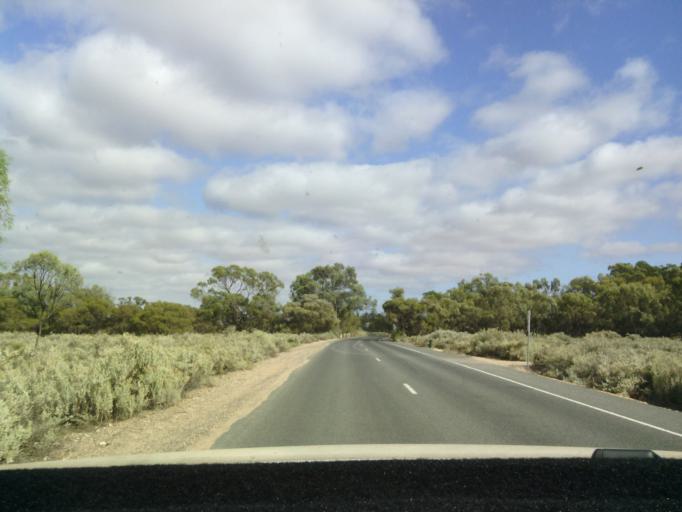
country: AU
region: South Australia
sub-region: Berri and Barmera
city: Berri
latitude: -34.2824
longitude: 140.6286
